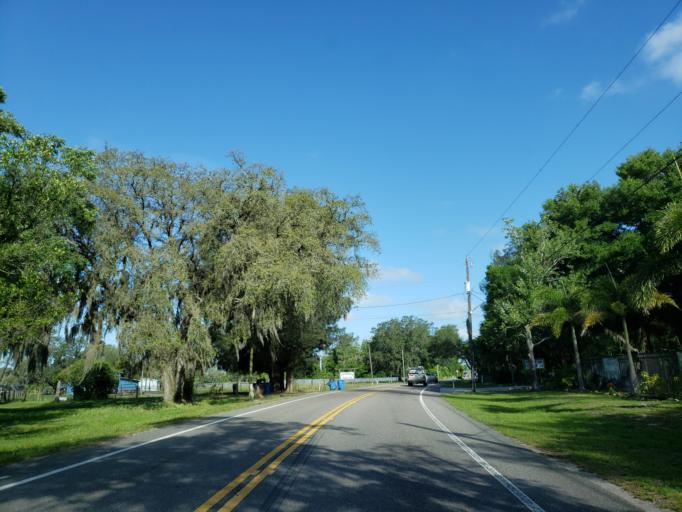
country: US
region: Florida
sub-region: Hillsborough County
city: Keystone
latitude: 28.1423
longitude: -82.6457
